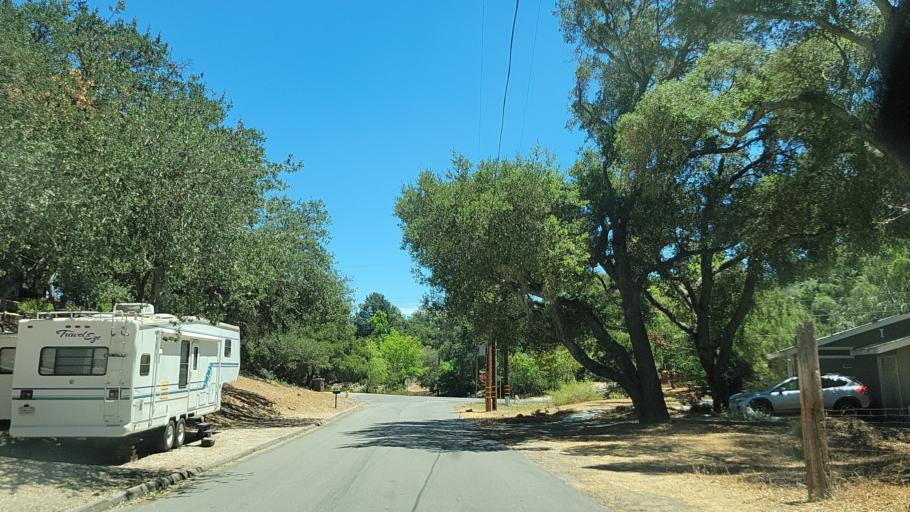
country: US
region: California
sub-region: San Luis Obispo County
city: Atascadero
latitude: 35.4976
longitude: -120.6755
